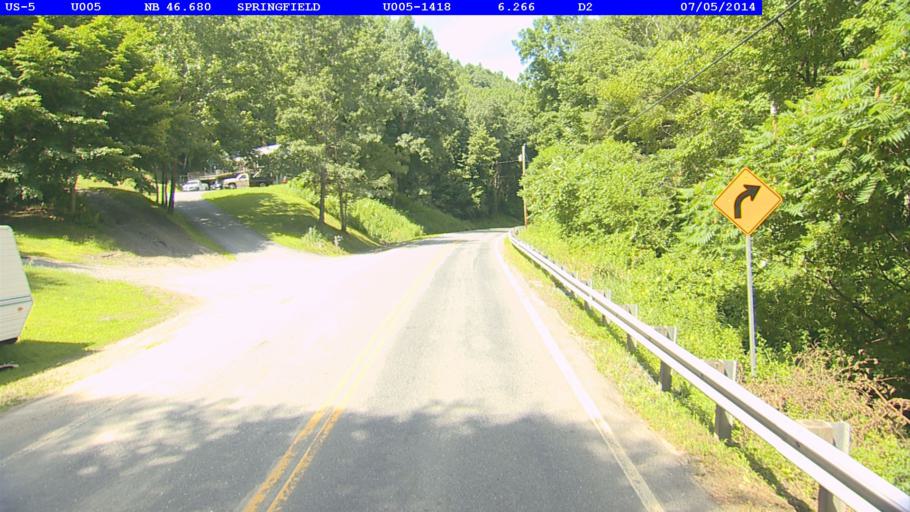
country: US
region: New Hampshire
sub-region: Sullivan County
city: Charlestown
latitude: 43.3017
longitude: -72.4034
